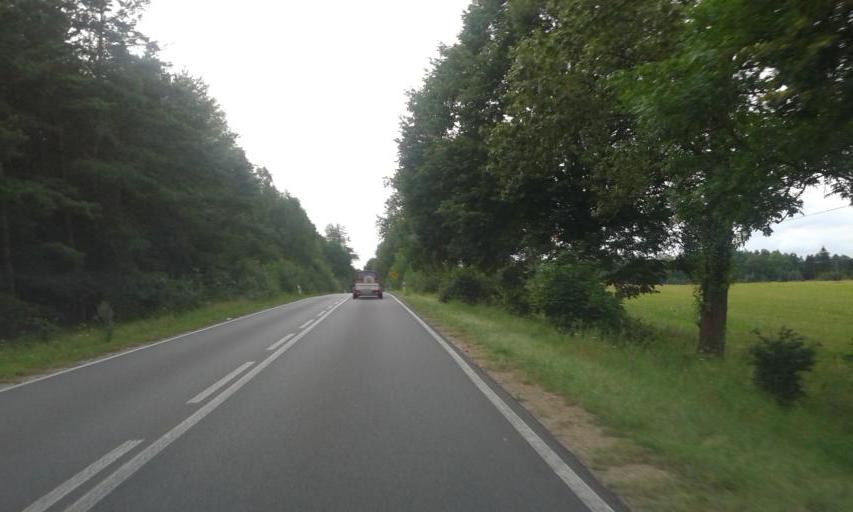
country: PL
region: West Pomeranian Voivodeship
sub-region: Powiat szczecinecki
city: Szczecinek
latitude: 53.7165
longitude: 16.5646
